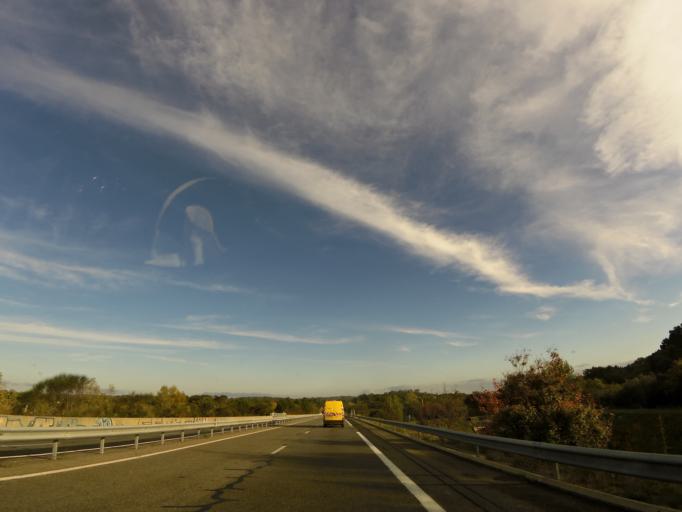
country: FR
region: Languedoc-Roussillon
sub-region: Departement du Gard
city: Vezenobres
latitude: 44.0445
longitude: 4.1320
